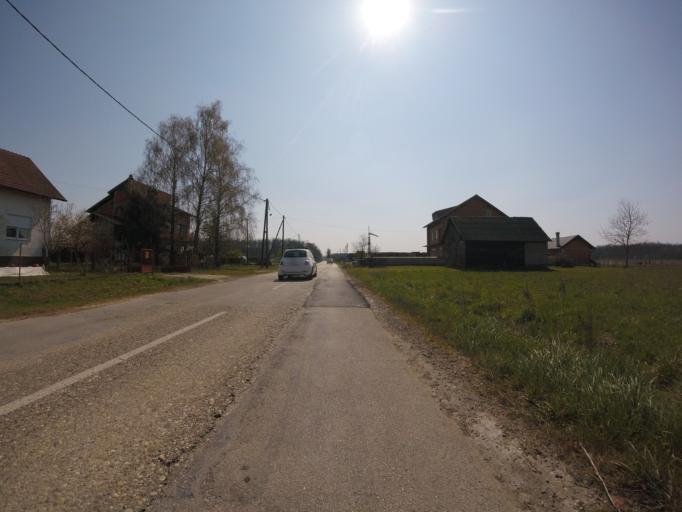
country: HR
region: Zagrebacka
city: Lukavec
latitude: 45.7003
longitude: 15.9861
